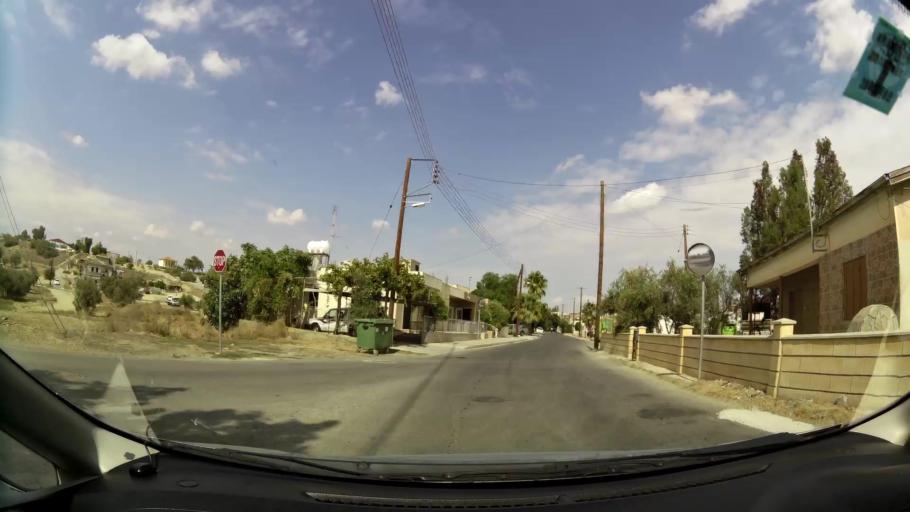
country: CY
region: Lefkosia
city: Tseri
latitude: 35.0694
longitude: 33.3229
